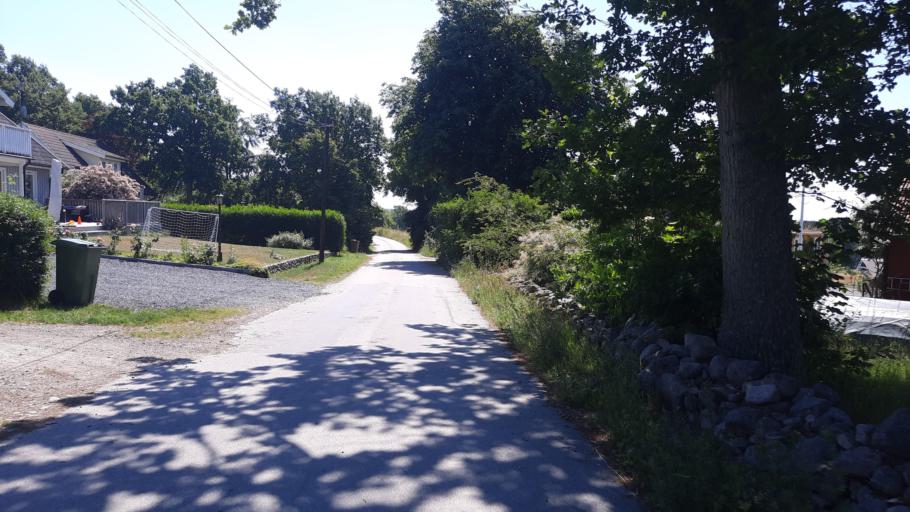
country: SE
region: Blekinge
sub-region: Karlskrona Kommun
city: Jaemjoe
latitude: 56.1477
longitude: 15.7705
